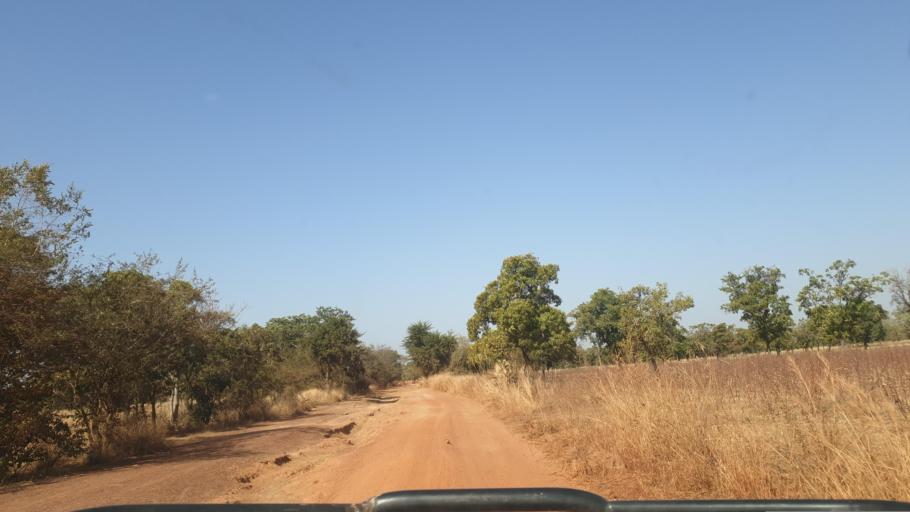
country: ML
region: Sikasso
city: Bougouni
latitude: 11.8210
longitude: -6.9656
